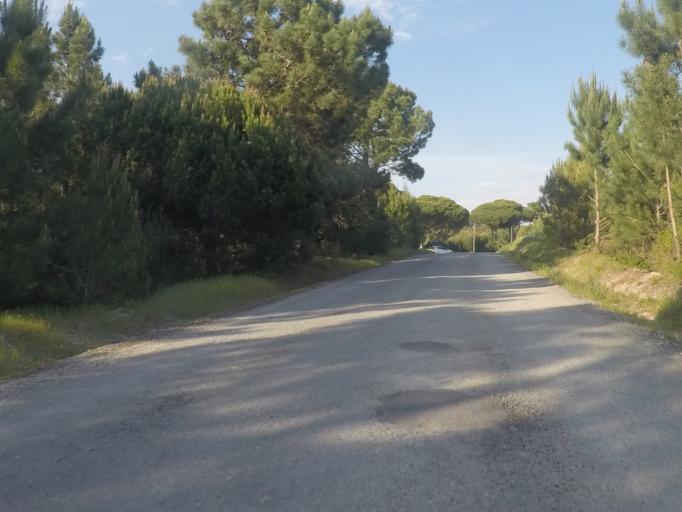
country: PT
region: Setubal
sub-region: Sesimbra
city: Sesimbra
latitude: 38.4592
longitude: -9.1860
